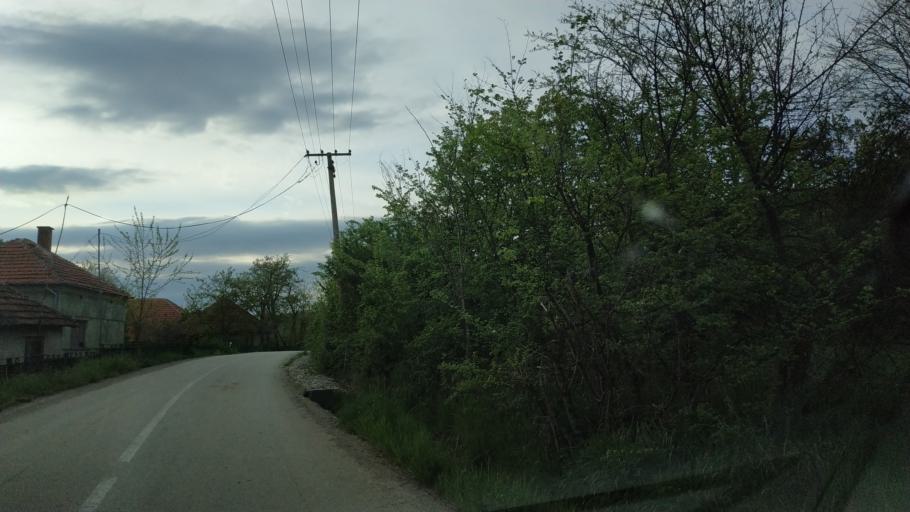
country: RS
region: Central Serbia
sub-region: Zajecarski Okrug
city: Soko Banja
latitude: 43.5257
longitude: 21.8582
